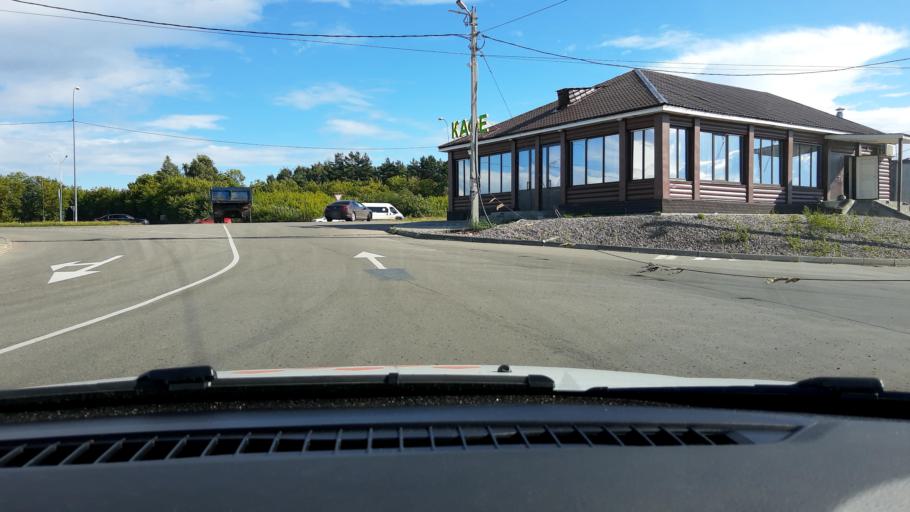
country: RU
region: Nizjnij Novgorod
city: Burevestnik
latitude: 56.1686
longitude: 43.7330
